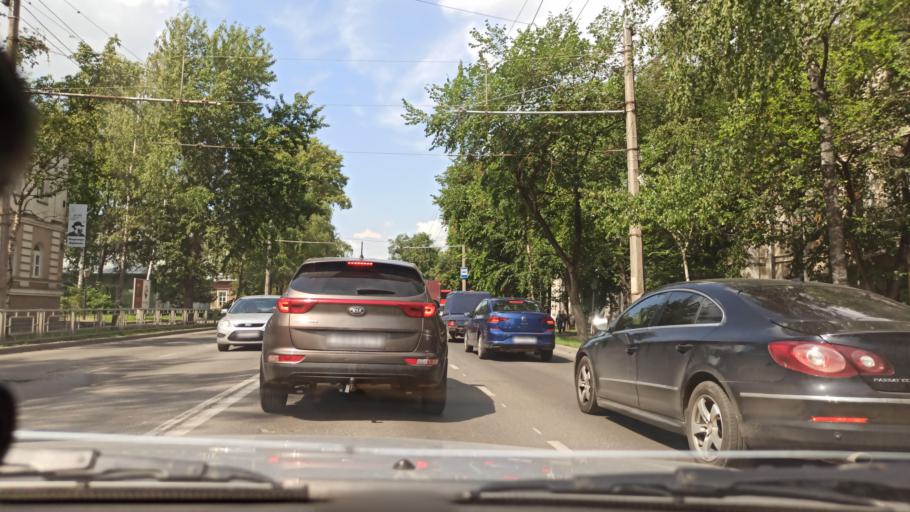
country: RU
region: Vologda
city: Vologda
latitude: 59.2188
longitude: 39.8801
